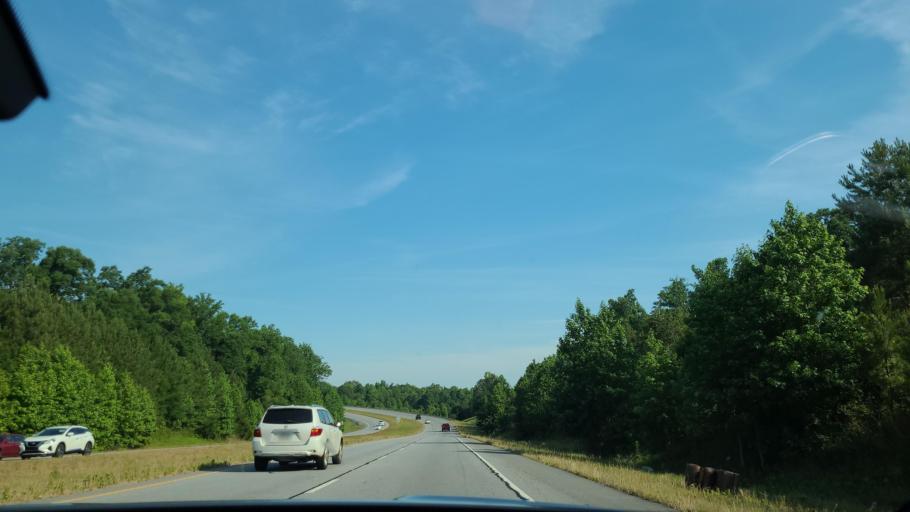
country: US
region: Georgia
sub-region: Jackson County
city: Nicholson
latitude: 34.0565
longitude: -83.4112
